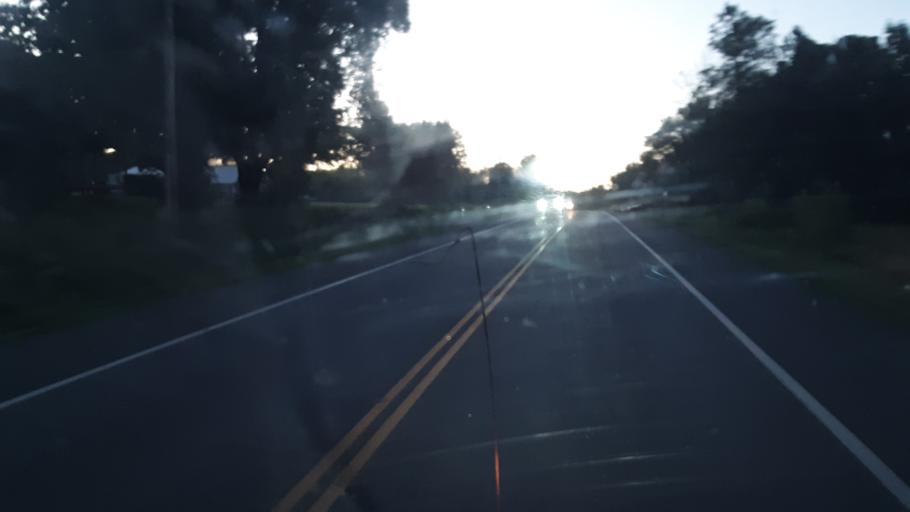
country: US
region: New York
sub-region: Montgomery County
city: Hagaman
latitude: 42.9506
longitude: -74.1266
